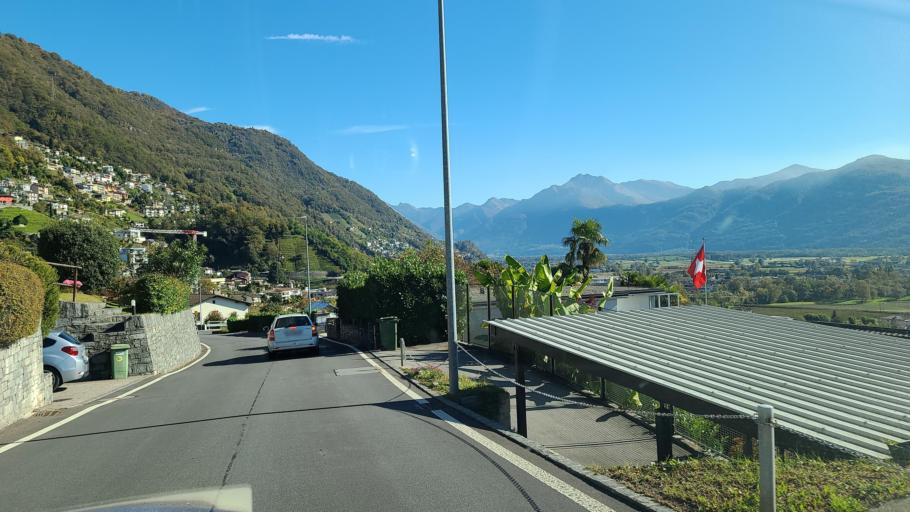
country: CH
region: Ticino
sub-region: Locarno District
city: Gordola
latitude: 46.1825
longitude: 8.8484
